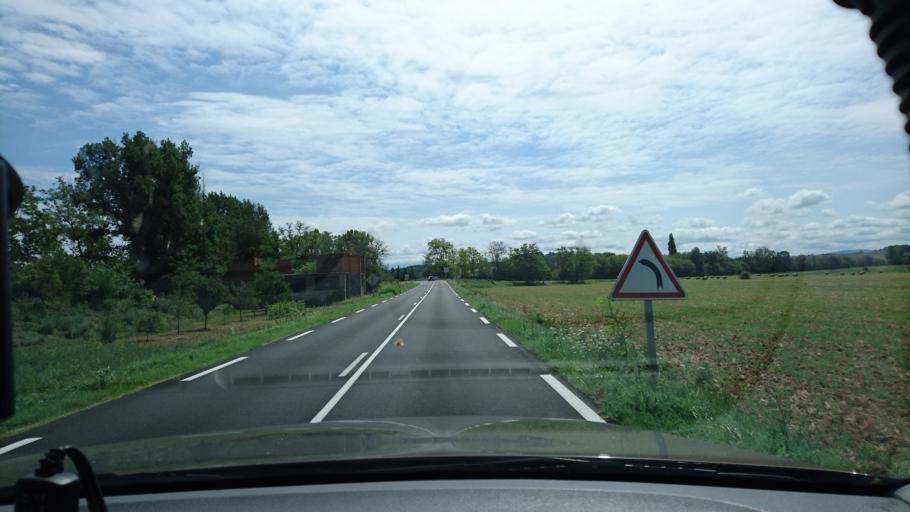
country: FR
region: Midi-Pyrenees
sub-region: Departement de l'Ariege
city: Lezat-sur-Leze
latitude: 43.2129
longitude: 1.3813
